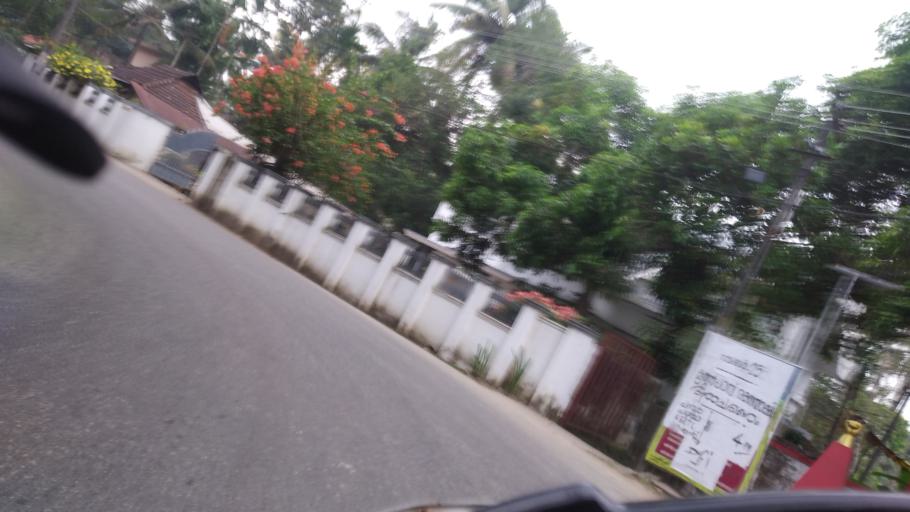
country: IN
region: Kerala
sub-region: Ernakulam
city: Elur
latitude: 10.1391
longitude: 76.2462
